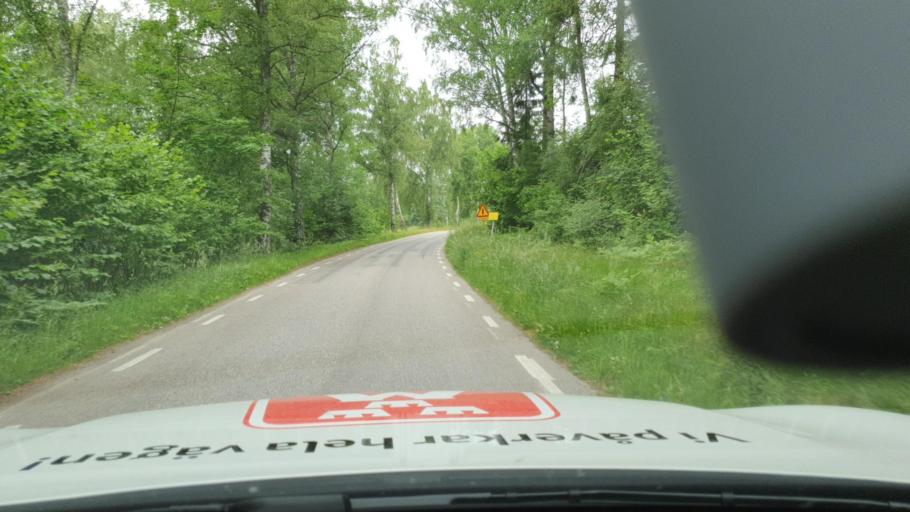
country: SE
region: Vaestra Goetaland
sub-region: Tibro Kommun
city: Tibro
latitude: 58.3494
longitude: 14.1567
